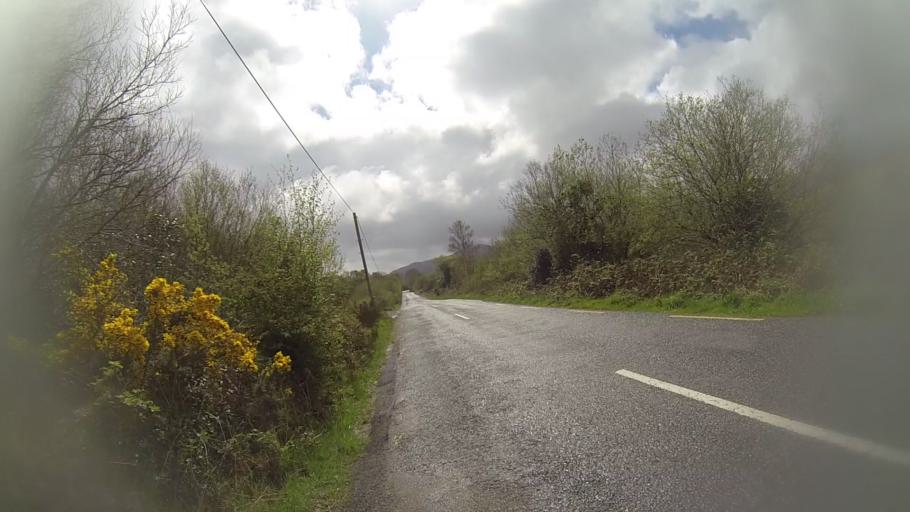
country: IE
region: Munster
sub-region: Ciarrai
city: Killorglin
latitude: 51.8425
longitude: -9.8920
